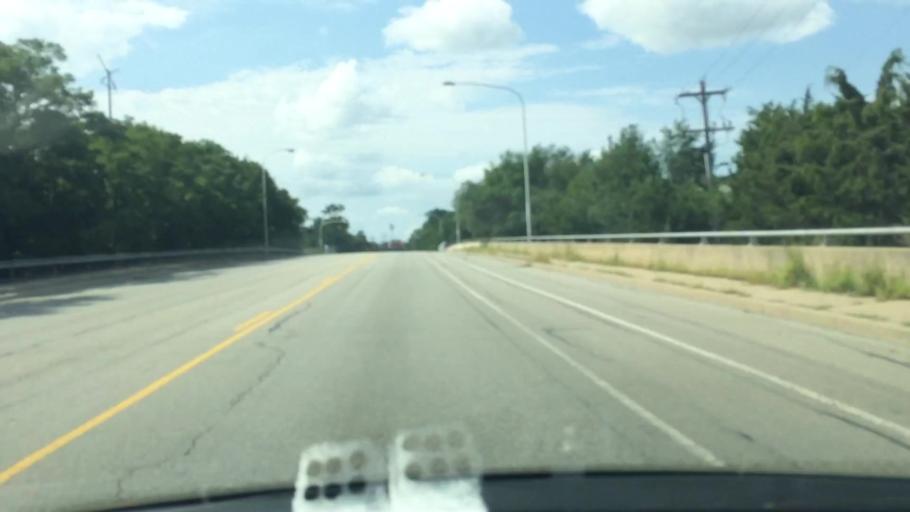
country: US
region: Pennsylvania
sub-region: Delaware County
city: Colwyn
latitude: 39.9189
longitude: -75.2203
